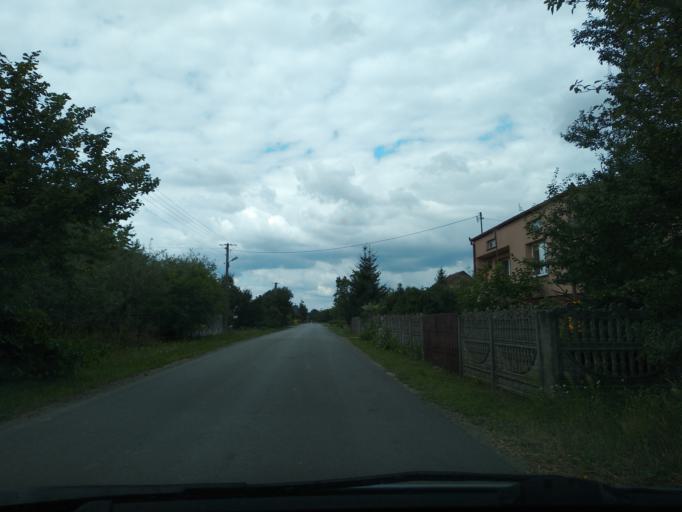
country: PL
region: Lublin Voivodeship
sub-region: Powiat lubartowski
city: Michow
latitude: 51.4955
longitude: 22.2896
